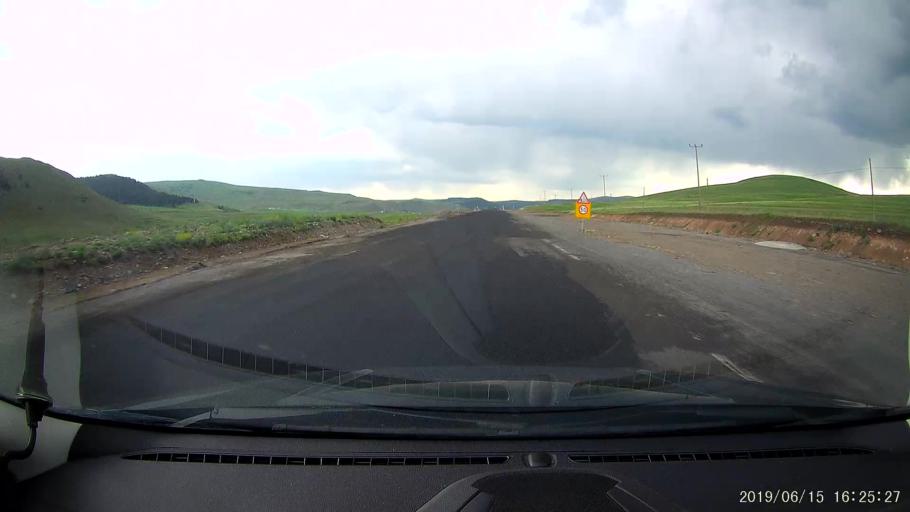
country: TR
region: Ardahan
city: Hanak
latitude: 41.1537
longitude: 42.8696
